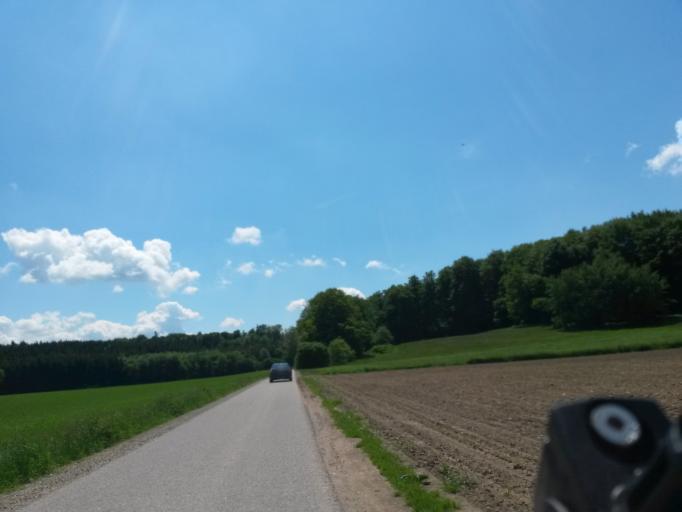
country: DE
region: Baden-Wuerttemberg
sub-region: Tuebingen Region
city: Bad Schussenried
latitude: 48.0229
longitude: 9.6935
